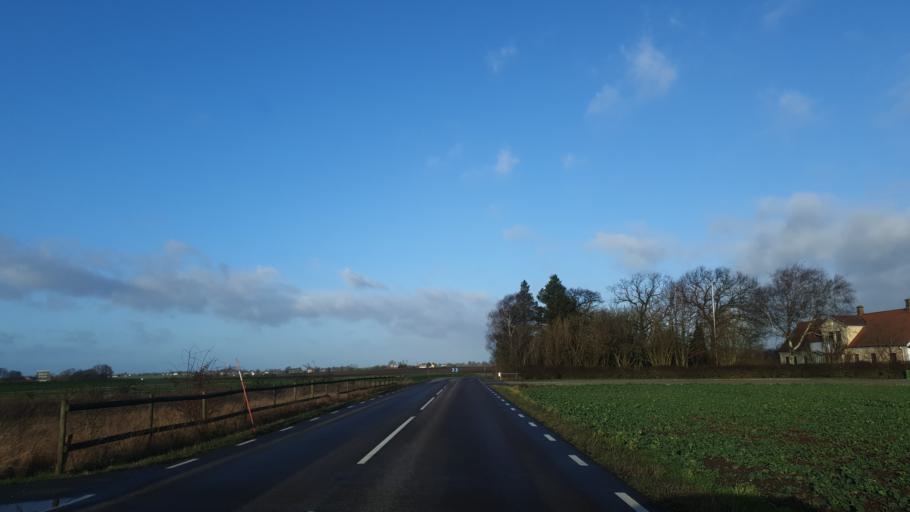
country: SE
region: Skane
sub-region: Vellinge Kommun
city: Vellinge
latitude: 55.4884
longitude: 13.0249
